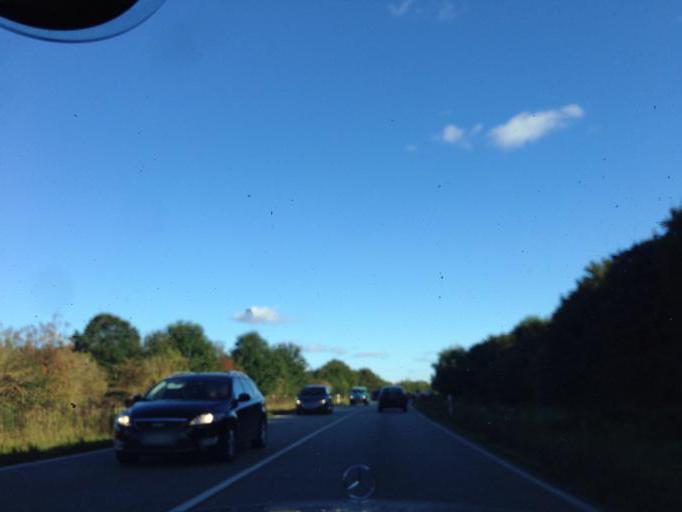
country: DE
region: Schleswig-Holstein
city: Boostedt
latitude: 54.0250
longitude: 10.0577
